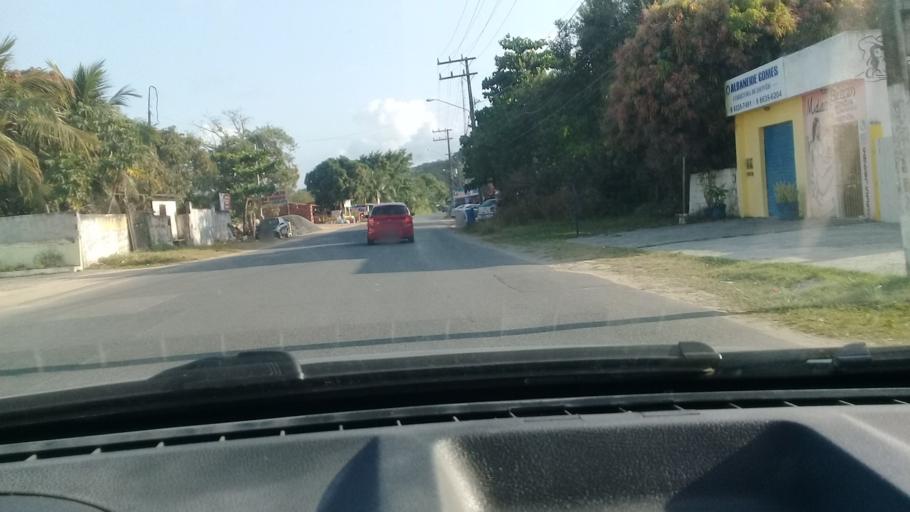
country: BR
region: Pernambuco
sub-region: Itamaraca
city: Itamaraca
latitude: -7.7706
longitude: -34.8360
